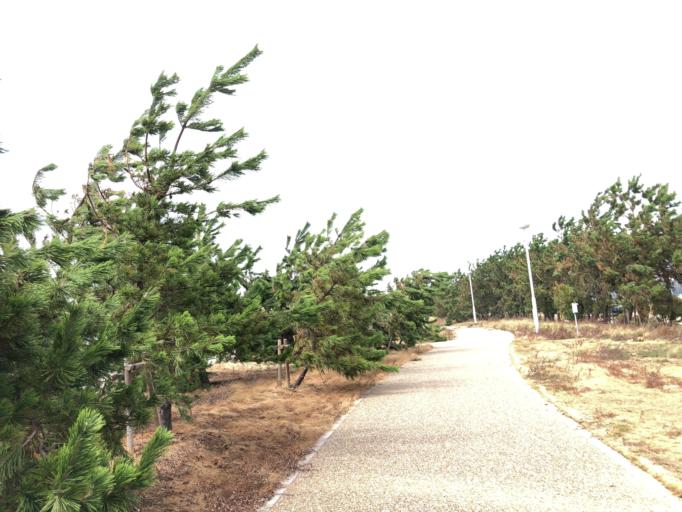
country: JP
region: Hyogo
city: Nishinomiya-hama
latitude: 34.7052
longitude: 135.3203
